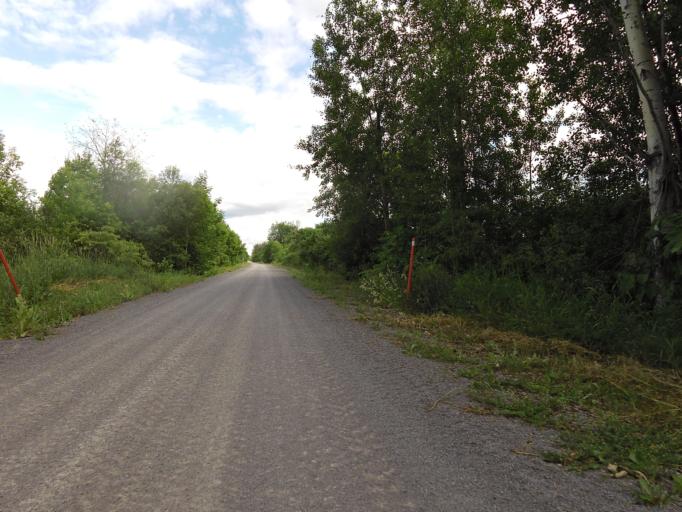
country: CA
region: Ontario
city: Arnprior
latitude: 45.3103
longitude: -76.2792
